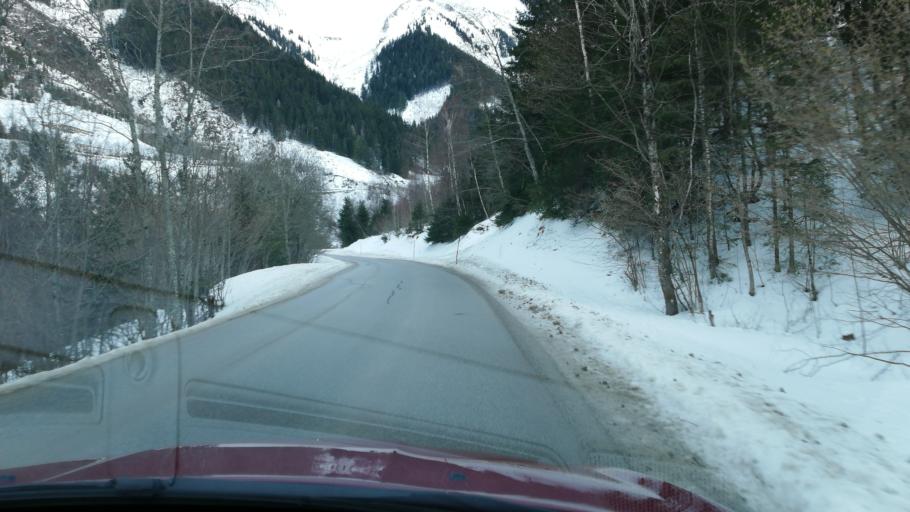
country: AT
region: Styria
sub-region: Politischer Bezirk Liezen
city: Donnersbach
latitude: 47.4334
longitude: 14.1563
